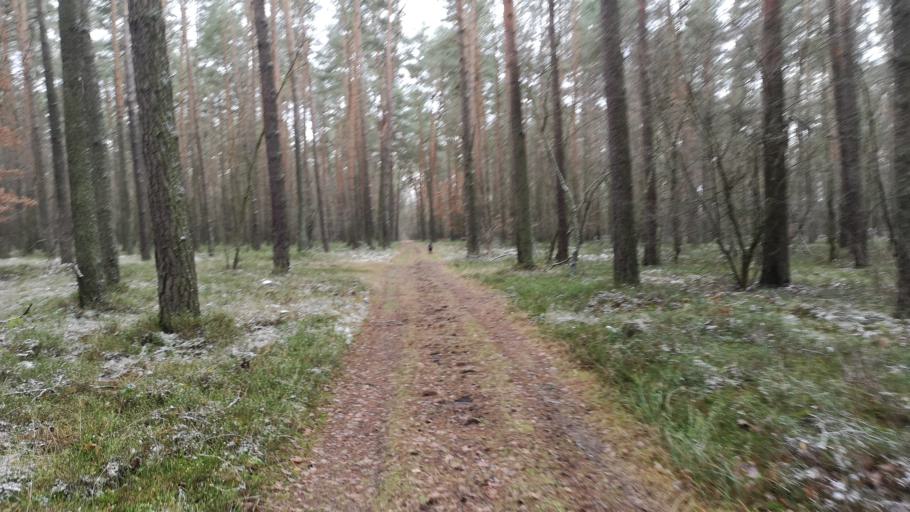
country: PL
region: Kujawsko-Pomorskie
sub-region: Powiat golubsko-dobrzynski
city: Ciechocin
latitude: 53.0800
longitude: 18.9614
